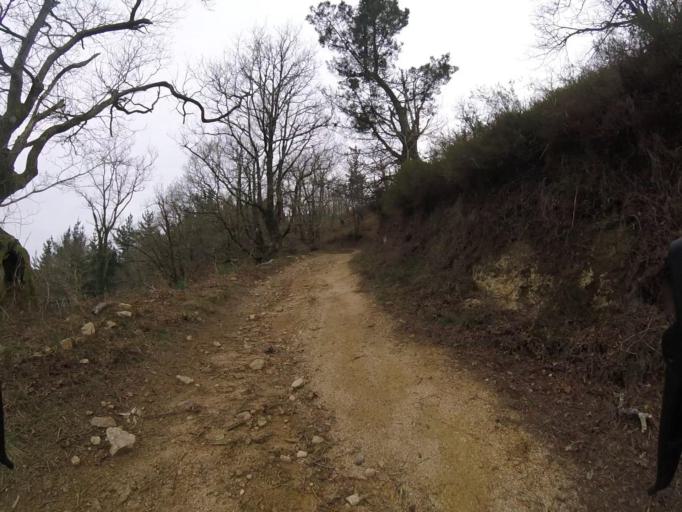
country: ES
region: Navarre
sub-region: Provincia de Navarra
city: Bera
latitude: 43.2891
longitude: -1.7391
